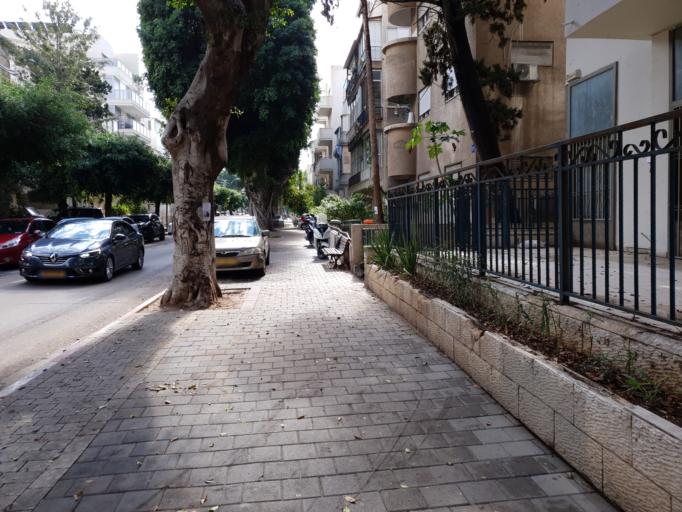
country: IL
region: Tel Aviv
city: Tel Aviv
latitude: 32.0810
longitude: 34.7755
